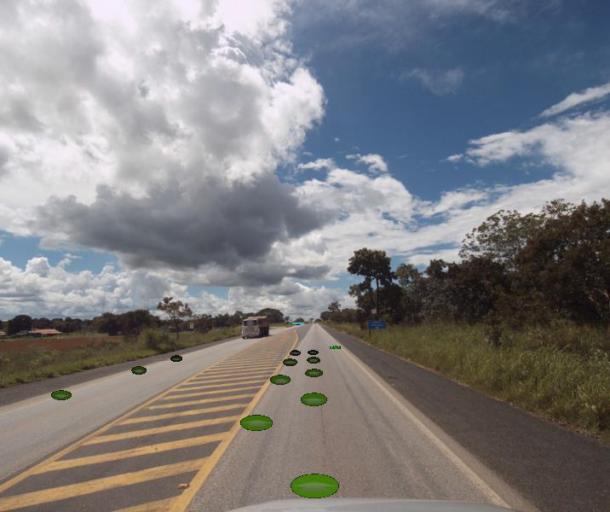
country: BR
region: Goias
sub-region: Uruacu
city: Uruacu
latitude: -14.0166
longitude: -49.0862
